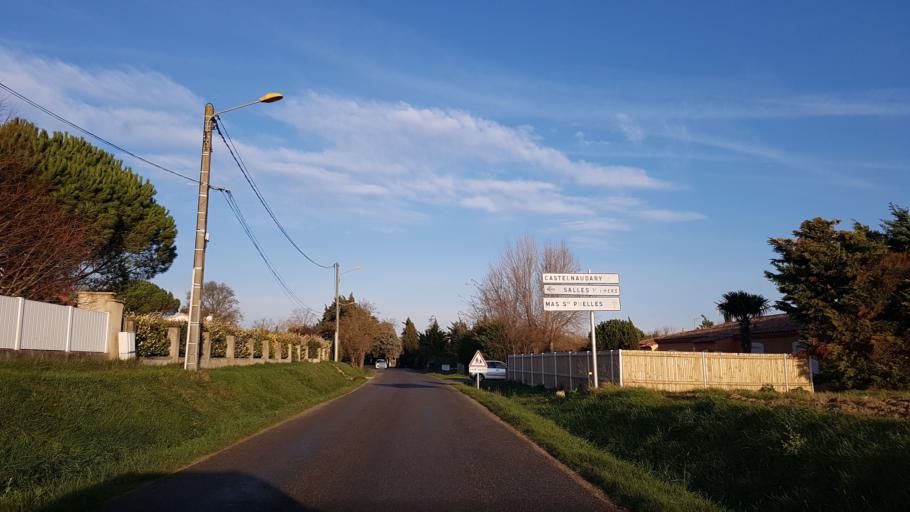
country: FR
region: Languedoc-Roussillon
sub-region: Departement de l'Aude
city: Villeneuve-la-Comptal
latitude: 43.2916
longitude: 1.9268
